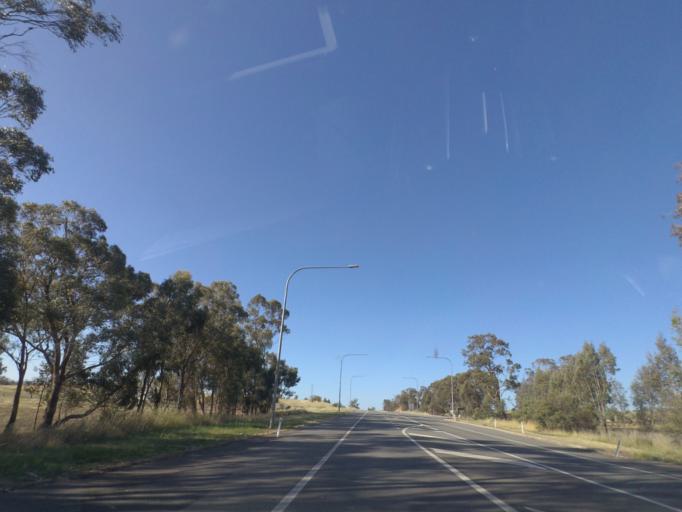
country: AU
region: New South Wales
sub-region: Wagga Wagga
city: Forest Hill
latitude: -35.2683
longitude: 147.7455
